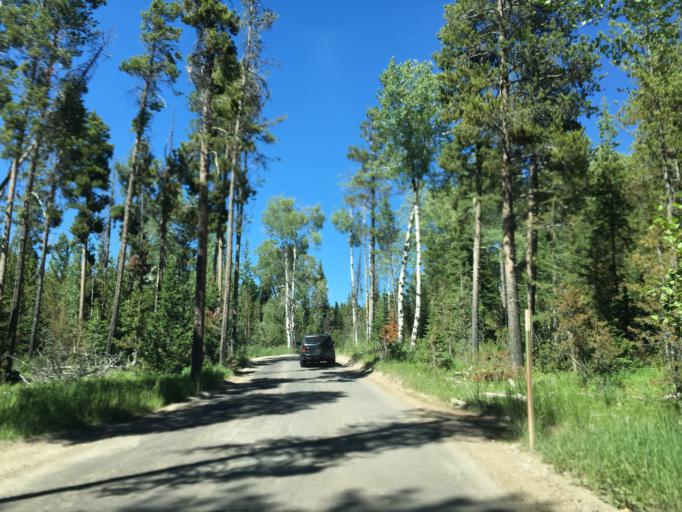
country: US
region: Wyoming
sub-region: Teton County
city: Moose Wilson Road
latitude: 43.6180
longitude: -110.7901
